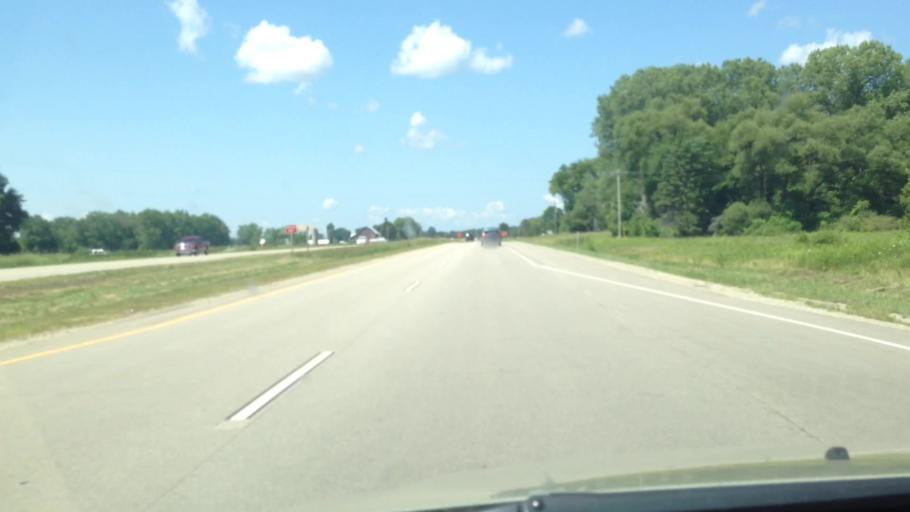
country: US
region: Wisconsin
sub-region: Oconto County
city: Oconto Falls
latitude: 44.8007
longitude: -88.0066
